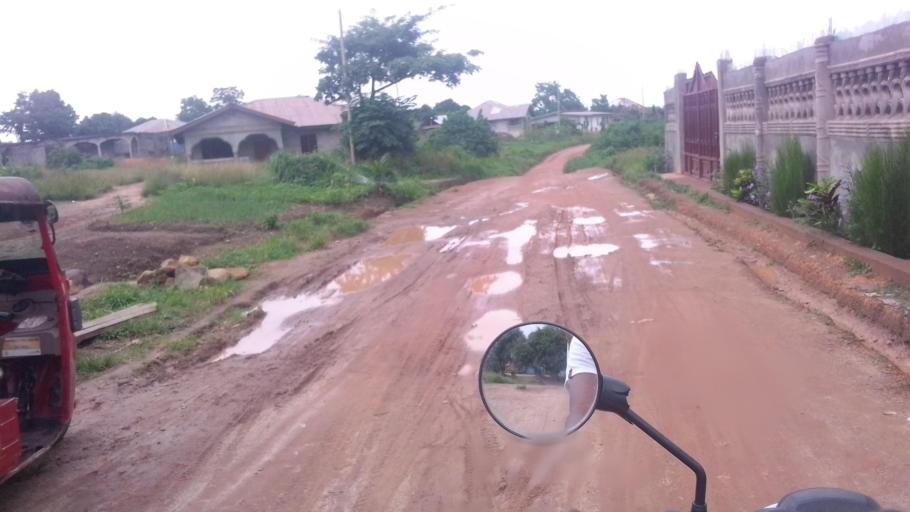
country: SL
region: Eastern Province
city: Kenema
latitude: 7.8614
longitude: -11.1710
